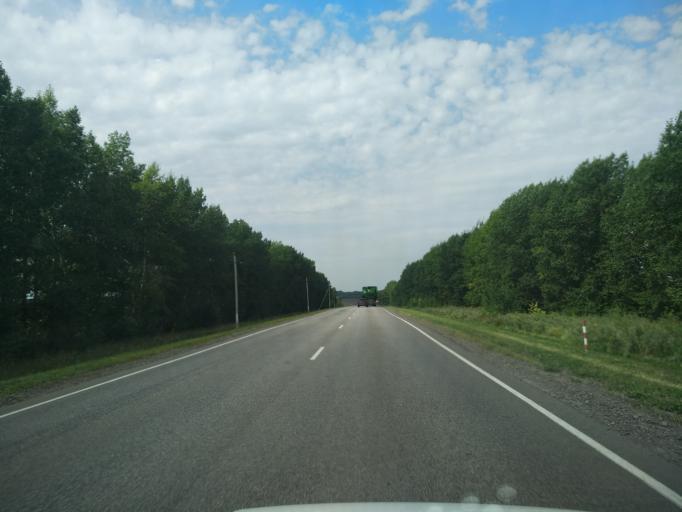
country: RU
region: Lipetsk
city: Dobrinka
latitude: 51.8903
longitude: 40.4389
